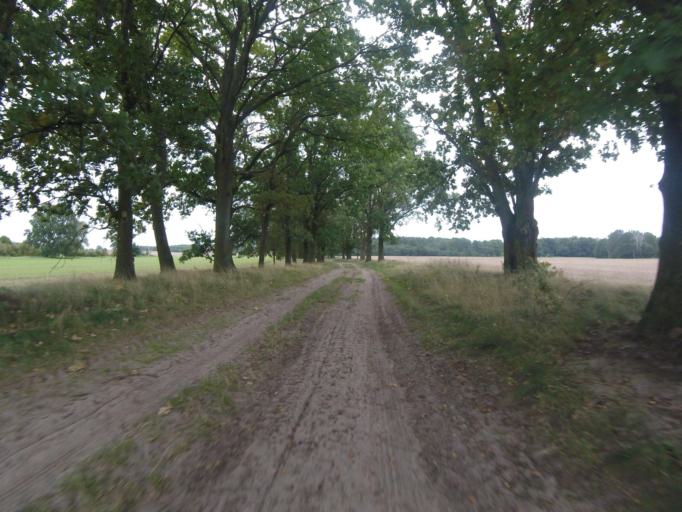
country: DE
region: Brandenburg
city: Mittenwalde
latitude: 52.2534
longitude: 13.5673
